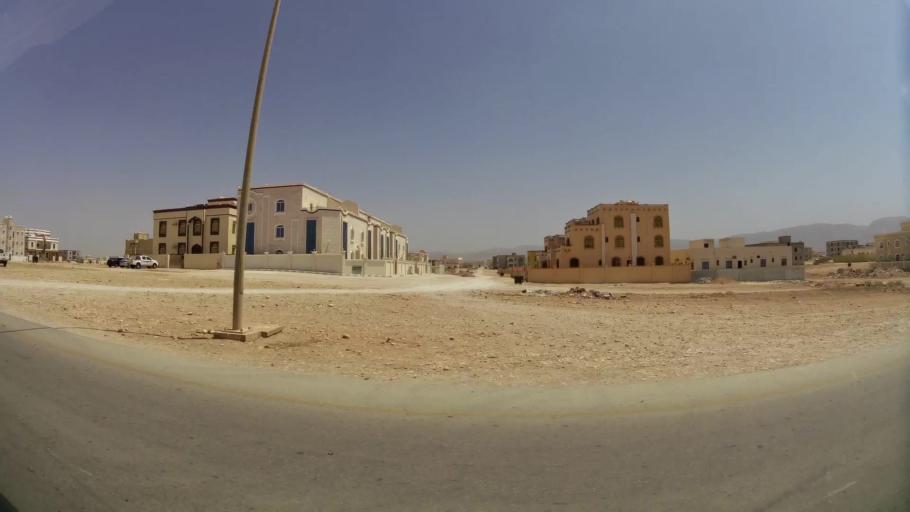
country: OM
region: Zufar
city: Salalah
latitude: 17.0683
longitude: 54.2121
